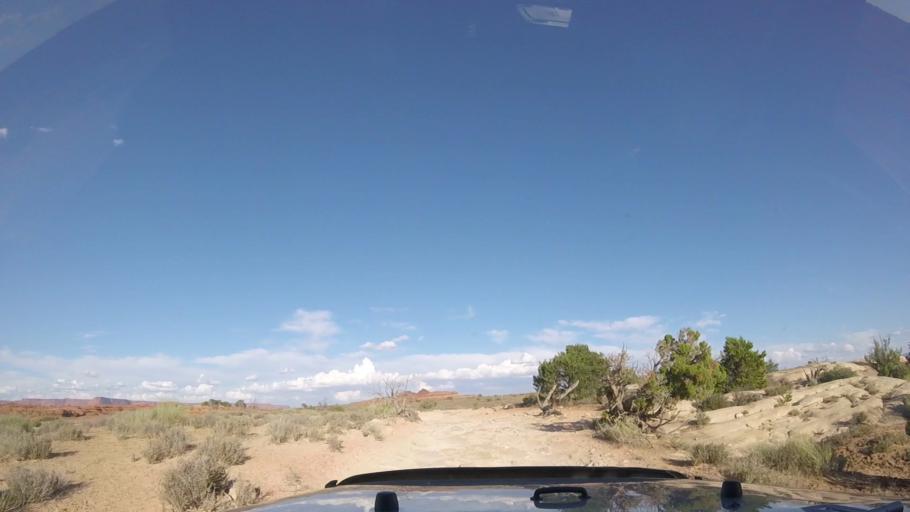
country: US
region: Utah
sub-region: Grand County
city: Moab
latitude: 38.2158
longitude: -109.7971
